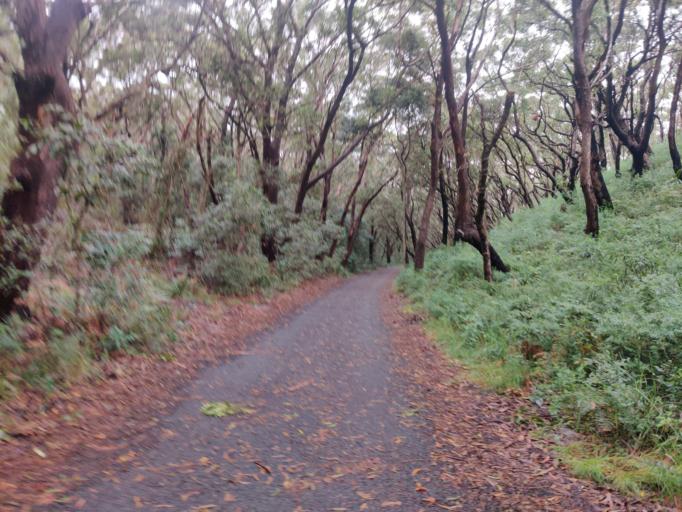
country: AU
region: New South Wales
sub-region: Great Lakes
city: Forster
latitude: -32.4373
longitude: 152.5367
